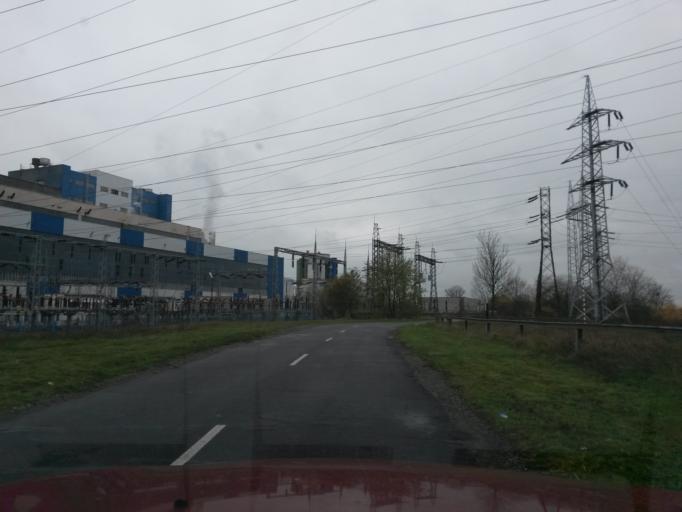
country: SK
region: Kosicky
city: Cierna nad Tisou
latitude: 48.5546
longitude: 21.9720
